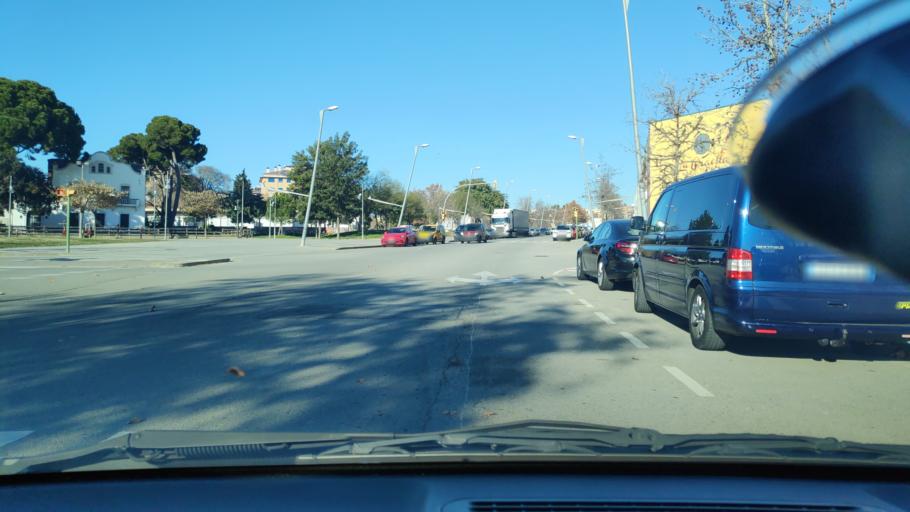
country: ES
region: Catalonia
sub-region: Provincia de Barcelona
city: Sant Quirze del Valles
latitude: 41.5423
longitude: 2.0917
